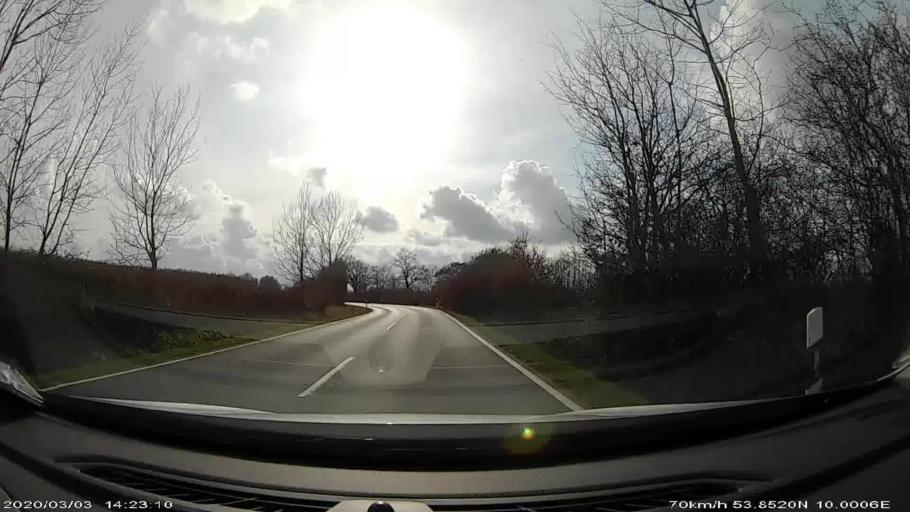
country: DE
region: Schleswig-Holstein
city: Kattendorf
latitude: 53.8518
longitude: 10.0005
